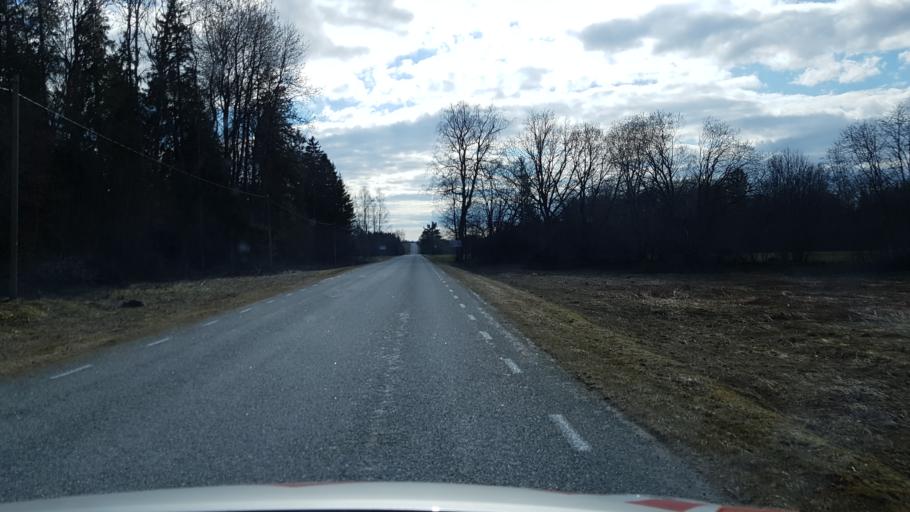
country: EE
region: Laeaene-Virumaa
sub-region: Kadrina vald
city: Kadrina
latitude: 59.3082
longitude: 26.2309
